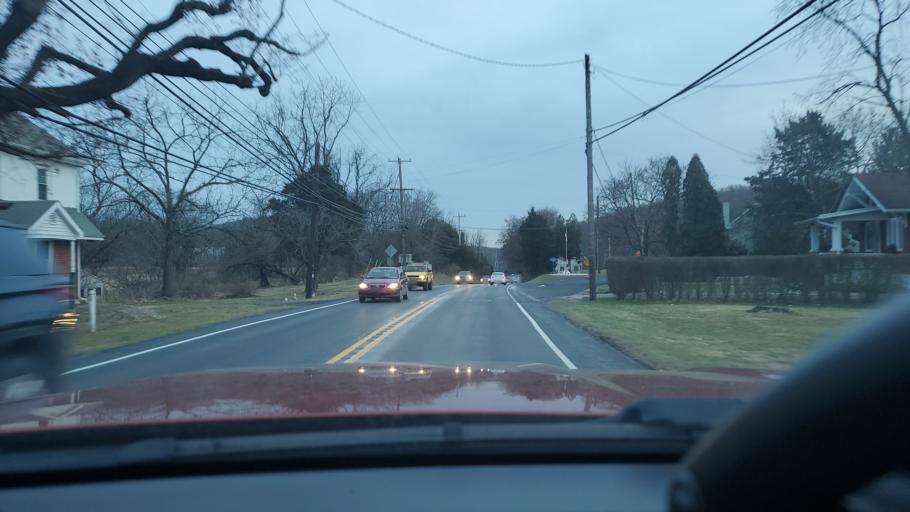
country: US
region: Pennsylvania
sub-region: Montgomery County
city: Spring Mount
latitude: 40.2754
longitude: -75.4770
